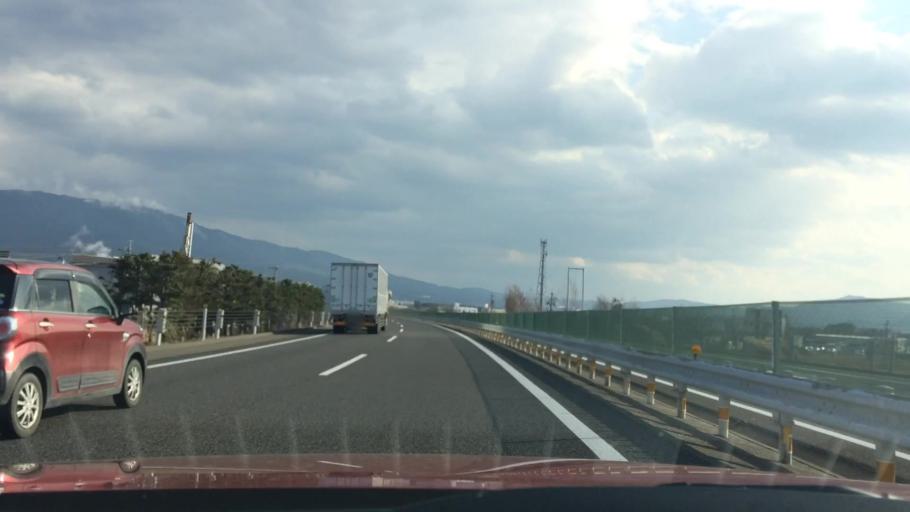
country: JP
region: Nagano
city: Matsumoto
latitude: 36.1737
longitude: 137.9434
